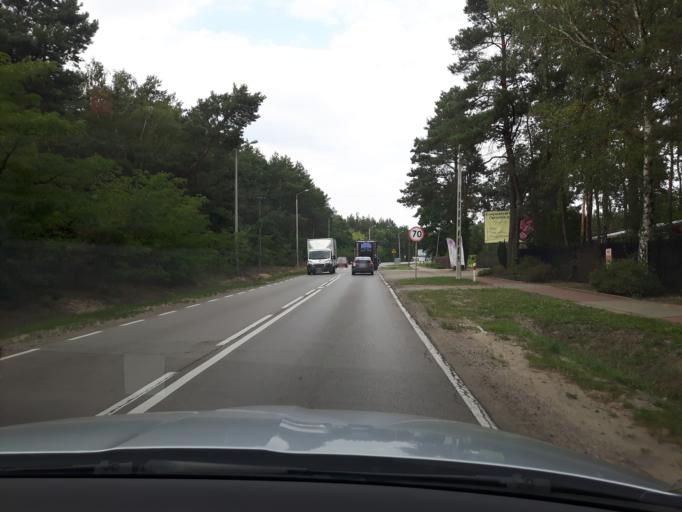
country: PL
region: Masovian Voivodeship
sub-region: Powiat legionowski
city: Stanislawow Pierwszy
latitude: 52.3819
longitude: 21.0292
